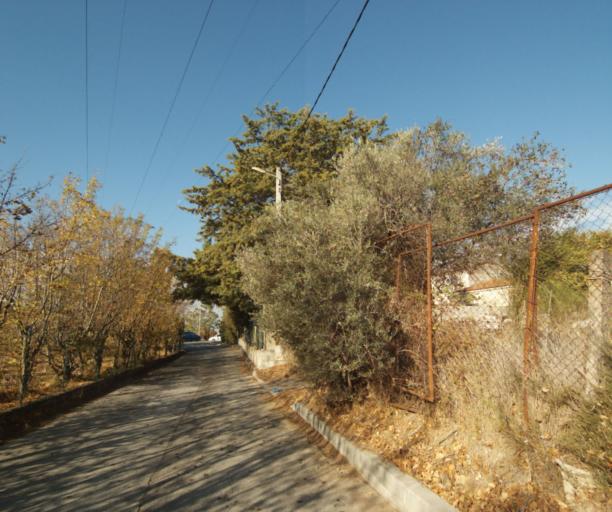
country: FR
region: Provence-Alpes-Cote d'Azur
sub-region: Departement des Bouches-du-Rhone
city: Allauch
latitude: 43.3219
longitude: 5.4939
